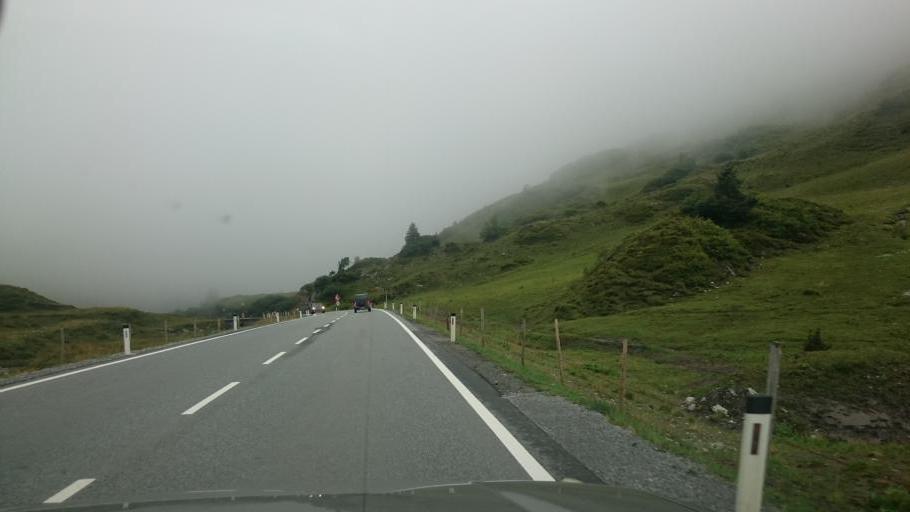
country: AT
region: Vorarlberg
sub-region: Politischer Bezirk Bludenz
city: Lech
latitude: 47.1544
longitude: 10.1649
